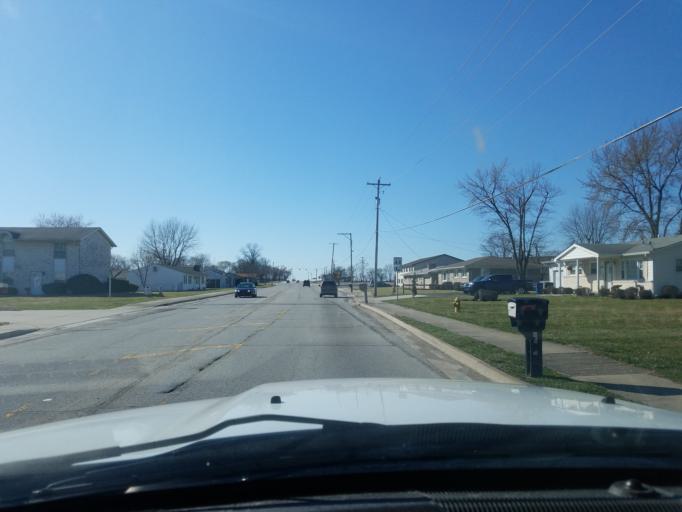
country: US
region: Indiana
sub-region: Shelby County
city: Shelbyville
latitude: 39.5046
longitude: -85.7989
